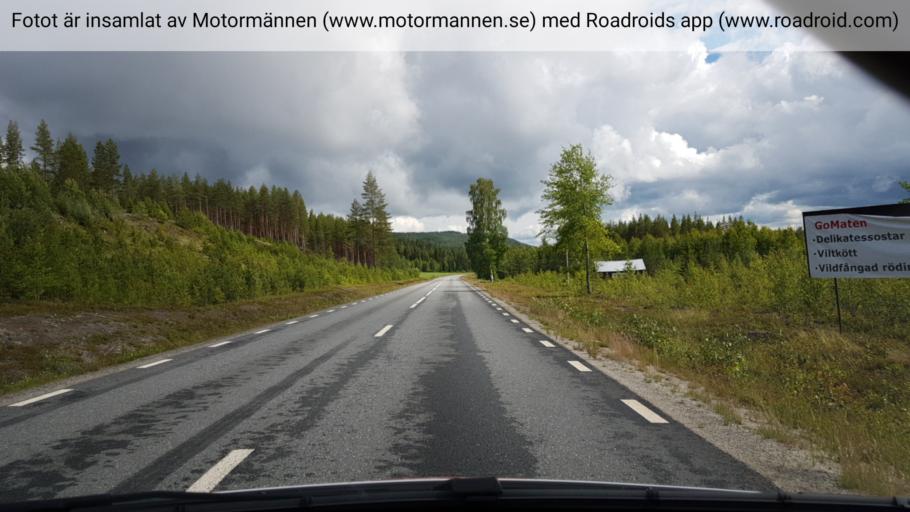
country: SE
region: Vaesterbotten
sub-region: Bjurholms Kommun
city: Bjurholm
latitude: 64.2819
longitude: 19.2341
